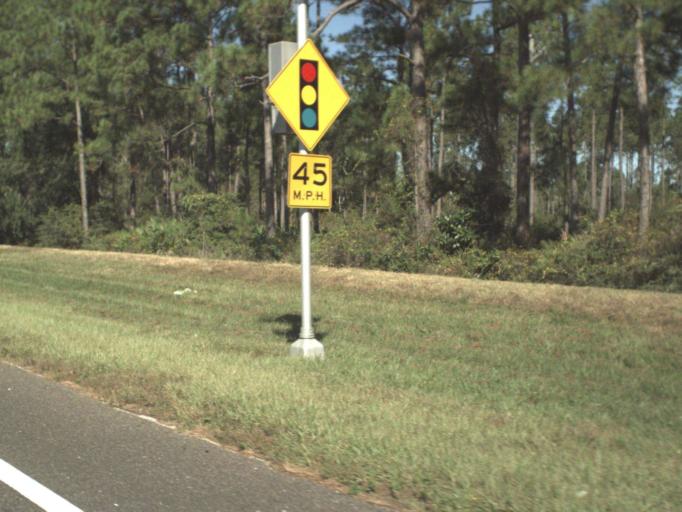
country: US
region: Florida
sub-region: Walton County
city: Seaside
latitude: 30.3585
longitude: -86.1518
